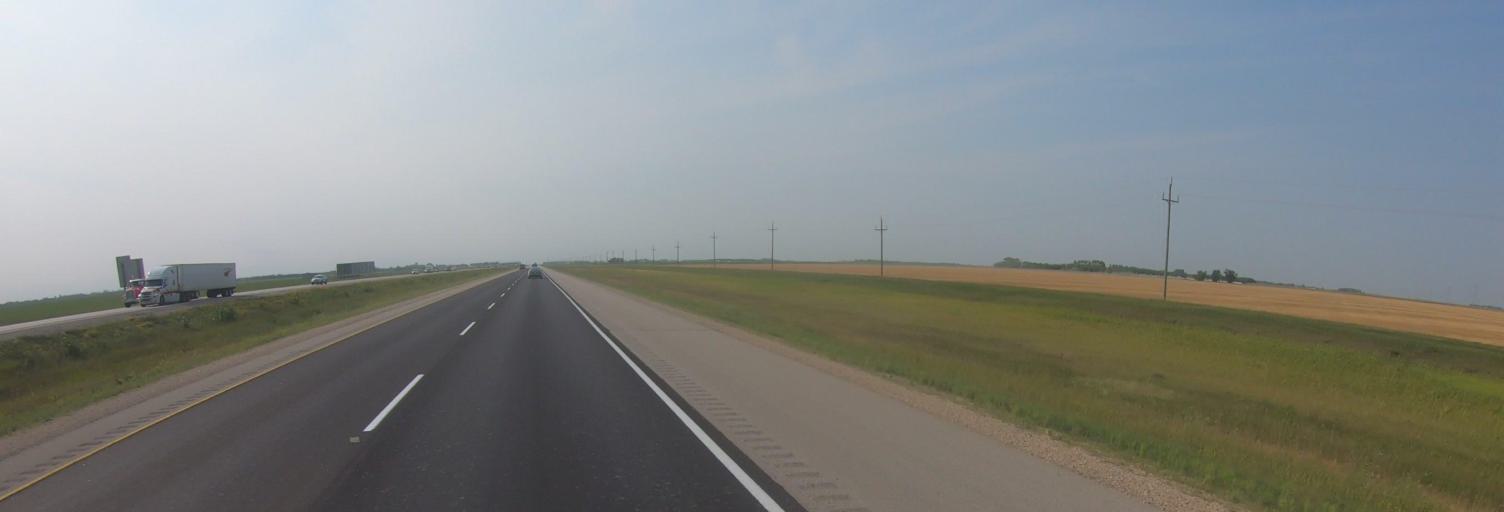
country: CA
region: Manitoba
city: Steinbach
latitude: 49.7146
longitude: -96.6777
